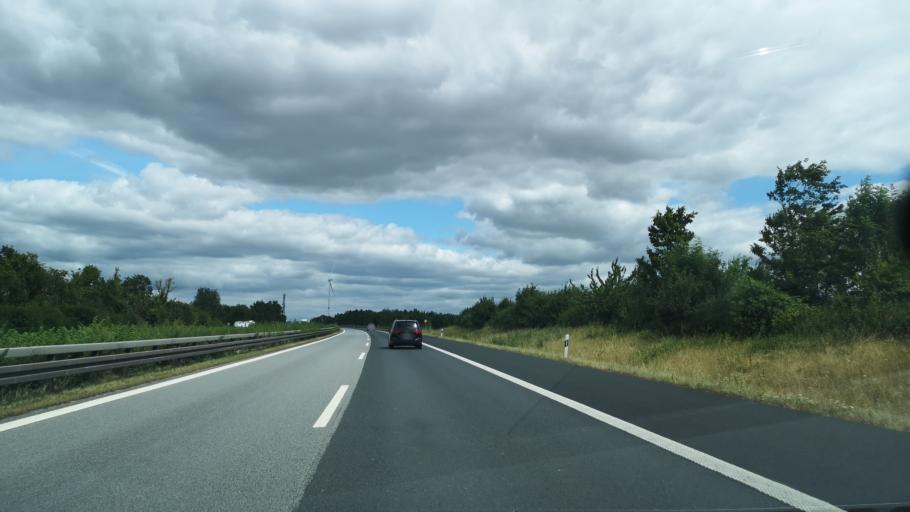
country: DE
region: Bavaria
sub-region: Regierungsbezirk Unterfranken
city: Werneck
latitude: 50.0248
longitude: 10.0697
